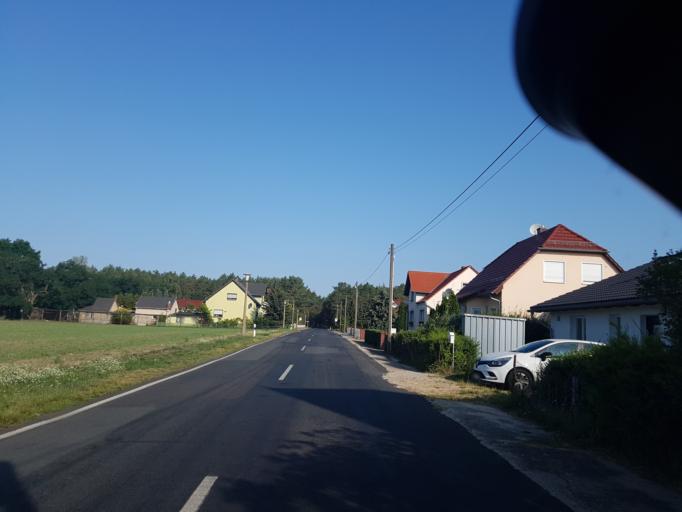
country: DE
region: Brandenburg
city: Niemegk
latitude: 52.1593
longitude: 12.6893
